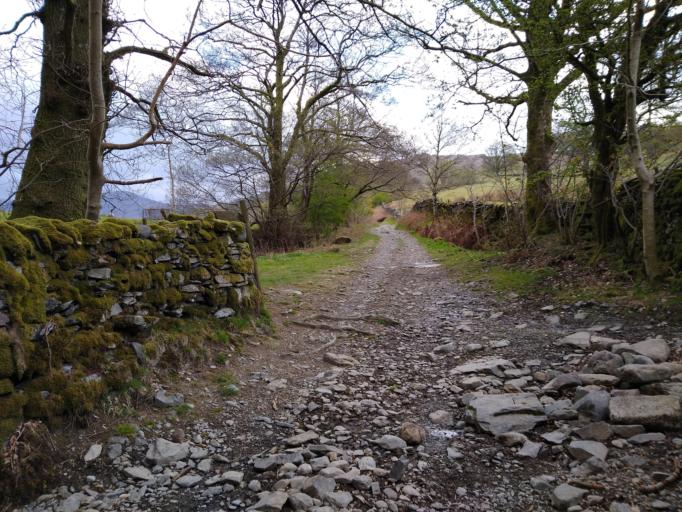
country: GB
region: England
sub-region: Cumbria
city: Windermere
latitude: 54.4138
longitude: -2.9050
